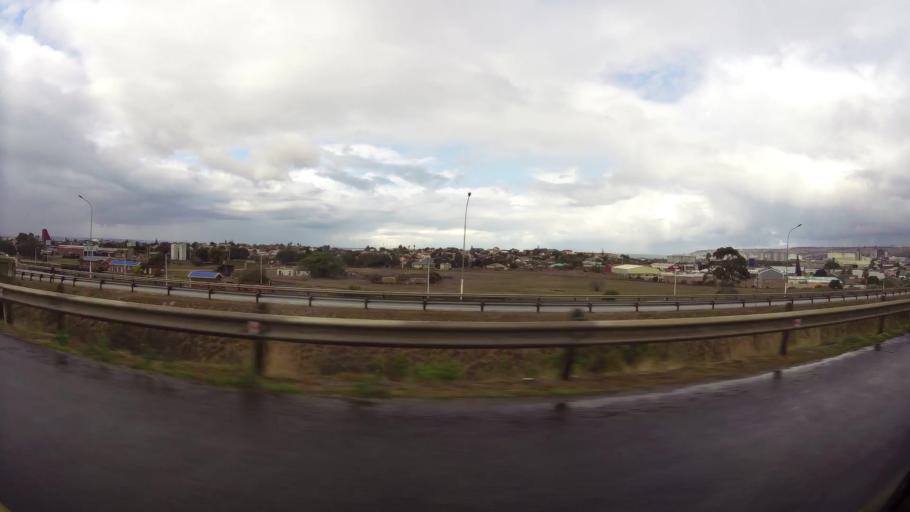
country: ZA
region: Western Cape
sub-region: Eden District Municipality
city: Mossel Bay
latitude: -34.1383
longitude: 22.1009
